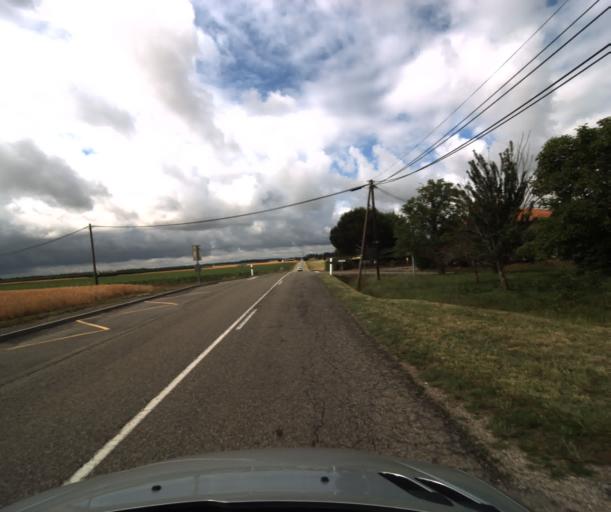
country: FR
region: Midi-Pyrenees
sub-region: Departement du Tarn-et-Garonne
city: Saint-Nicolas-de-la-Grave
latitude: 43.9992
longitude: 0.9868
